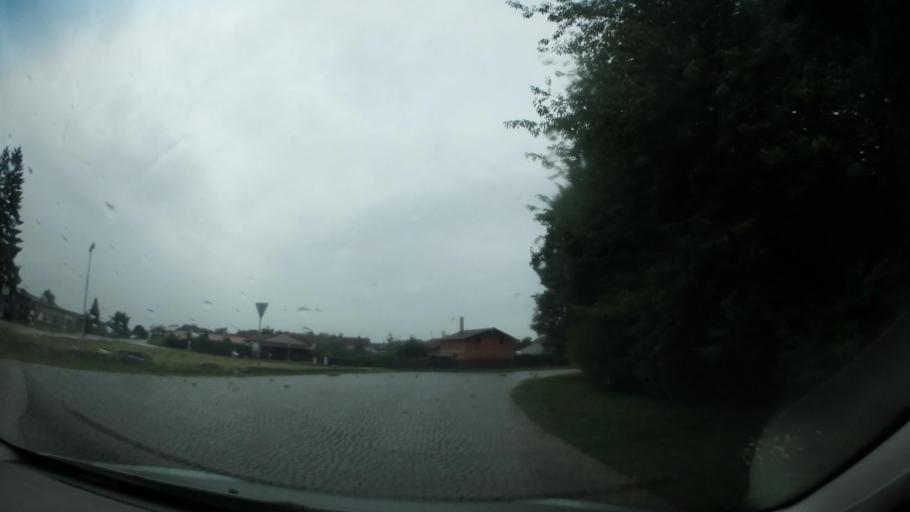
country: CZ
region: Central Bohemia
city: Milovice
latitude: 50.2308
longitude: 14.8960
